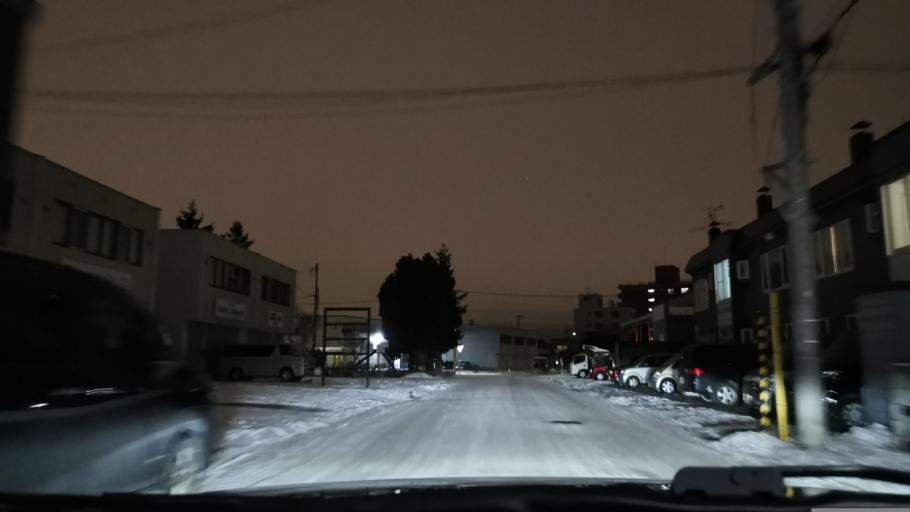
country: JP
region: Hokkaido
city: Sapporo
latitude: 43.0653
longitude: 141.3998
